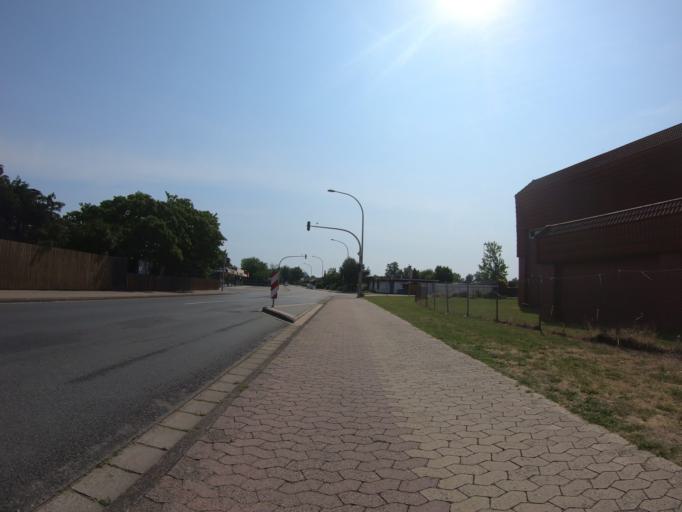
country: DE
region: Lower Saxony
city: Gifhorn
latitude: 52.4780
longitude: 10.5670
